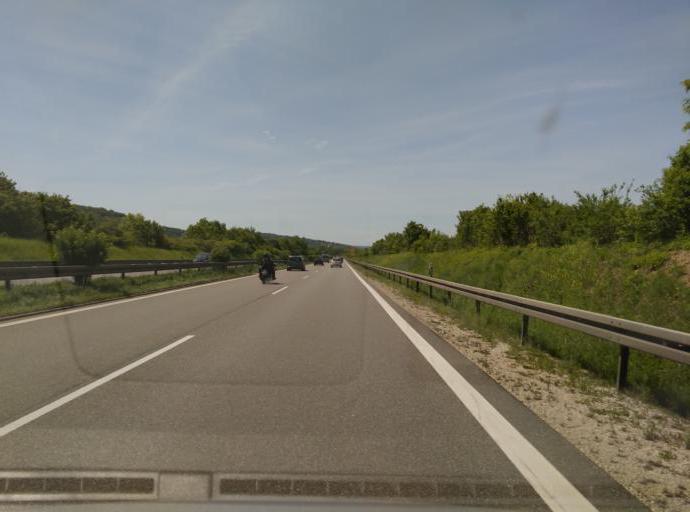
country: DE
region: Baden-Wuerttemberg
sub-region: Tuebingen Region
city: Kusterdingen
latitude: 48.5287
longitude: 9.1042
